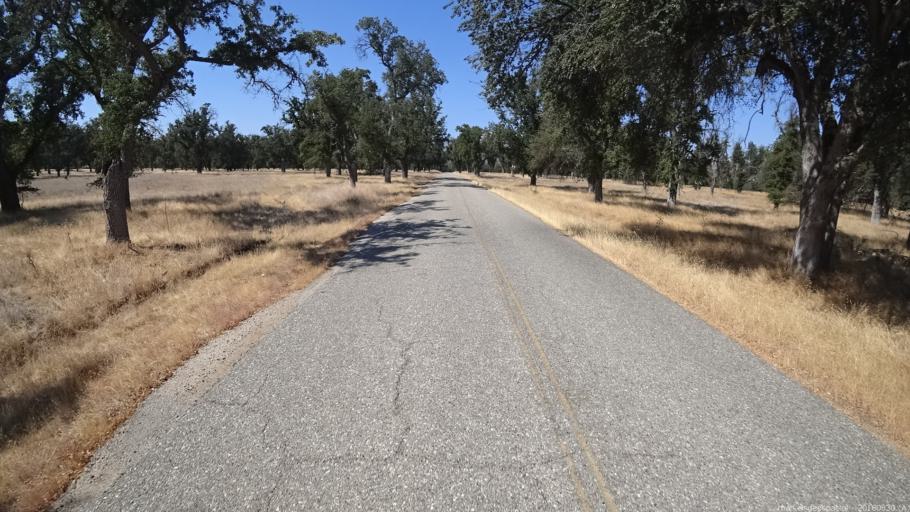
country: US
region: California
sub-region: Monterey County
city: King City
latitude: 36.0550
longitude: -121.3063
